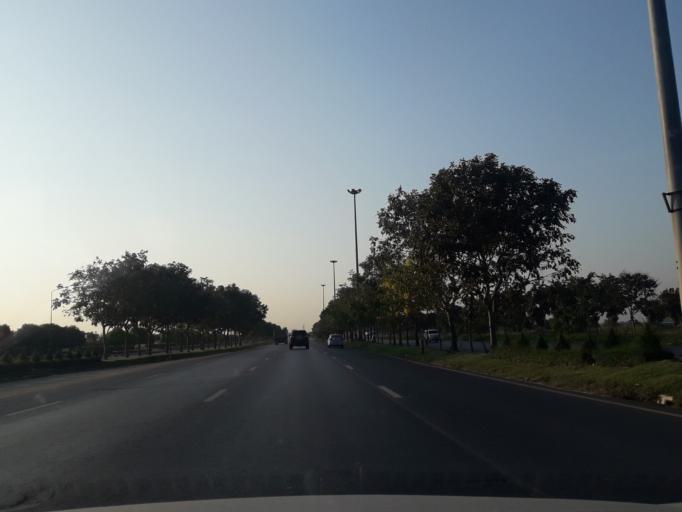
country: TH
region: Phra Nakhon Si Ayutthaya
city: Bang Pa-in
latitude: 14.2120
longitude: 100.5454
